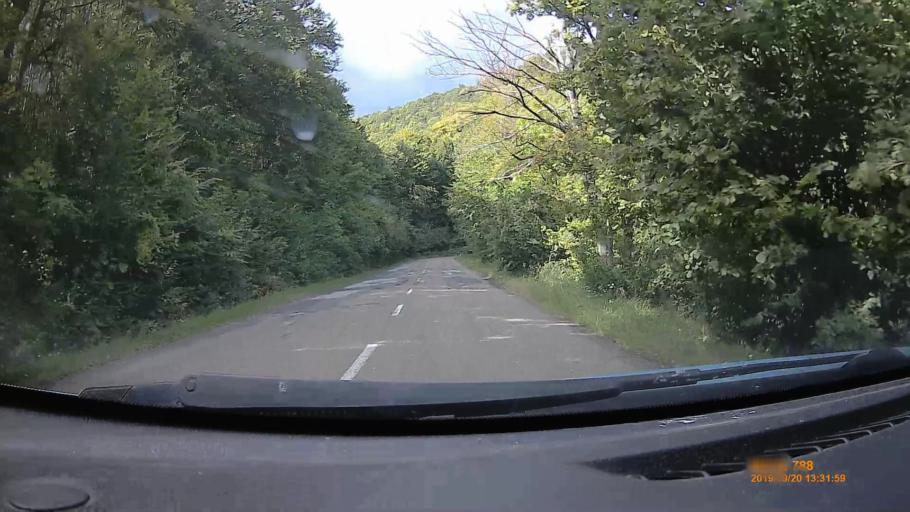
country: HU
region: Heves
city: Szilvasvarad
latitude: 48.0568
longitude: 20.4927
